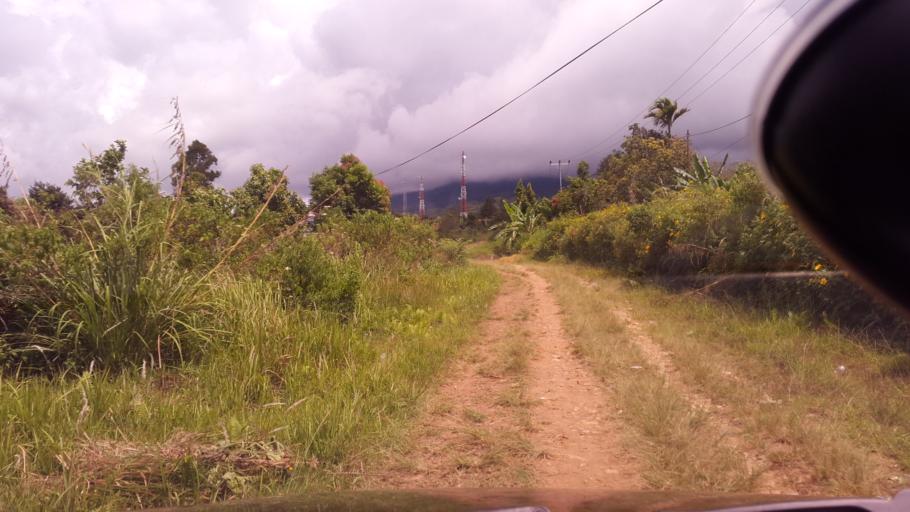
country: ID
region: West Sumatra
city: Gunung Talang
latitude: -0.9474
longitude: 100.6158
